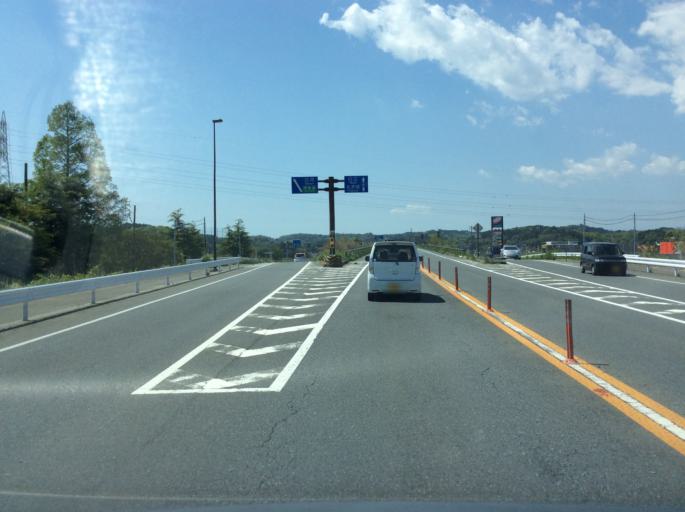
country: JP
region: Ibaraki
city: Kitaibaraki
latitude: 36.8963
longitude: 140.7889
